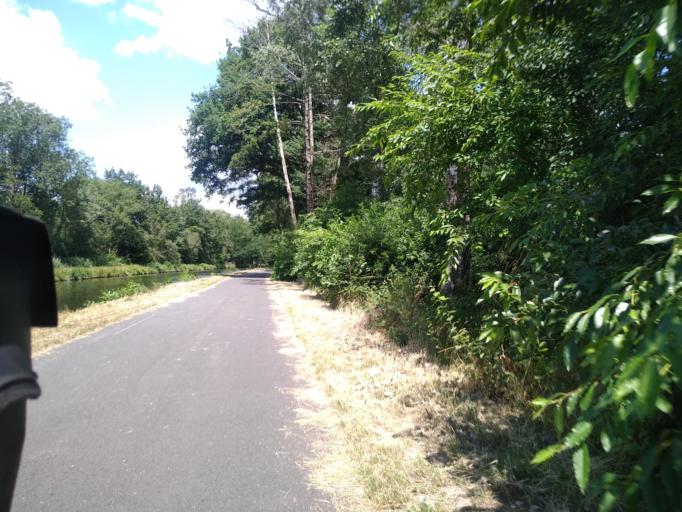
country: FR
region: Rhone-Alpes
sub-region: Departement de la Loire
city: Briennon
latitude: 46.1241
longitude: 4.0767
